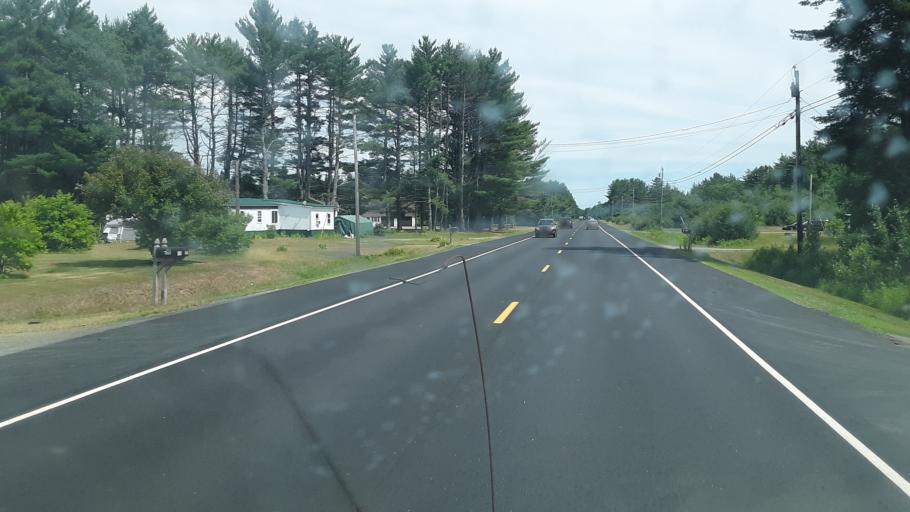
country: US
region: Maine
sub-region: Somerset County
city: Norridgewock
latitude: 44.6963
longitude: -69.7525
